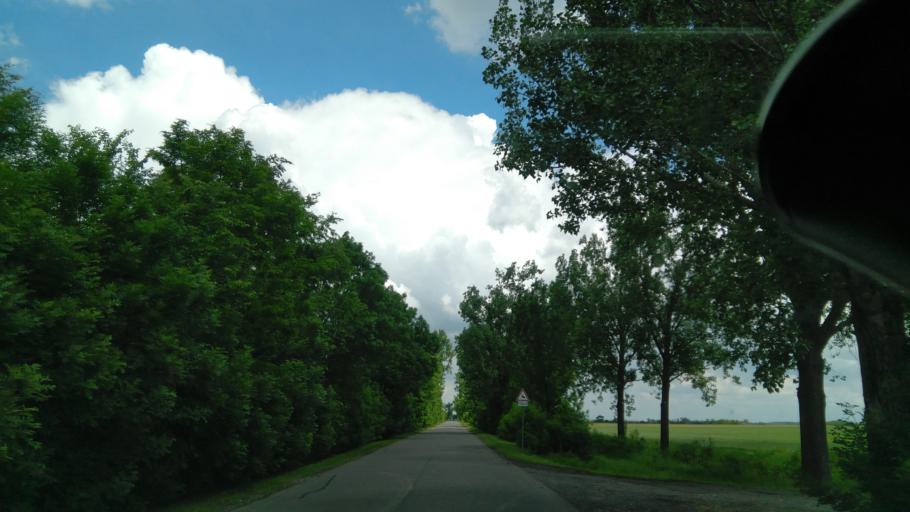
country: HU
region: Bekes
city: Gyomaendrod
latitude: 46.9863
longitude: 20.8944
